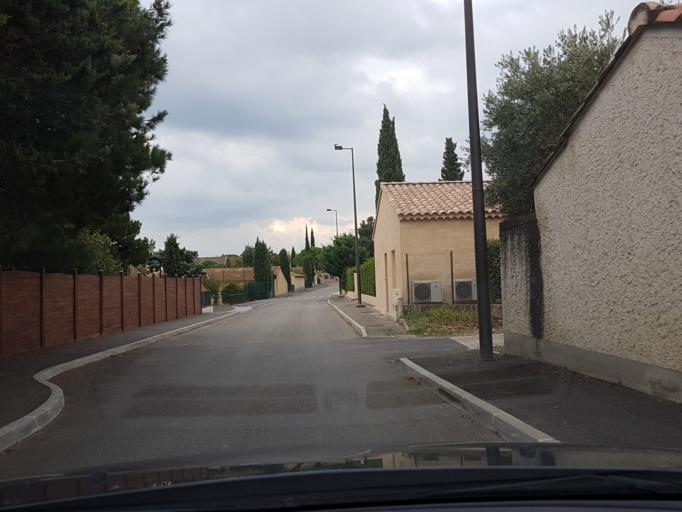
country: FR
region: Provence-Alpes-Cote d'Azur
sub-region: Departement du Vaucluse
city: Jonquerettes
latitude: 43.9499
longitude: 4.9341
